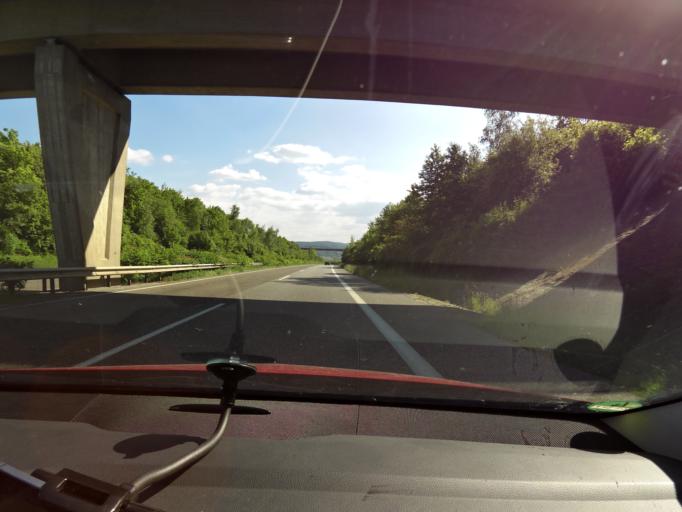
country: DE
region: Rheinland-Pfalz
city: Bad Neuenahr-Ahrweiler
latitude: 50.5648
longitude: 7.1189
